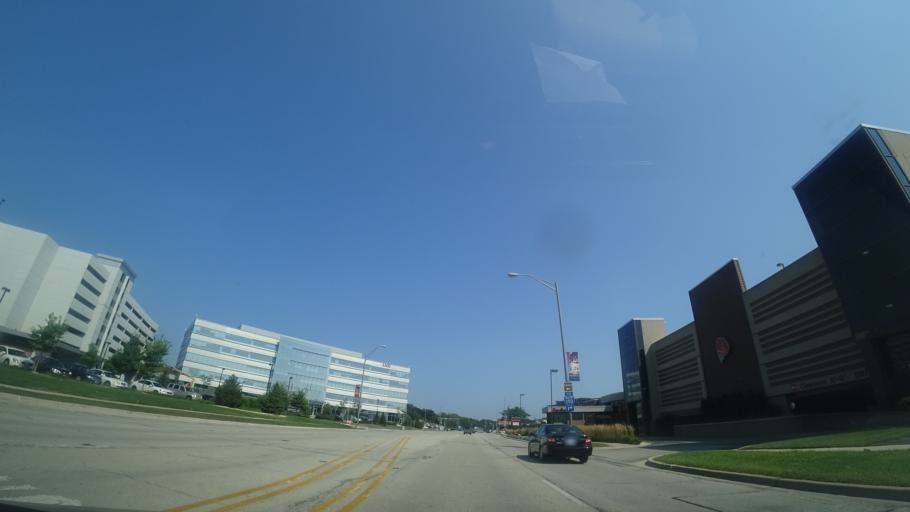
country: US
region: Illinois
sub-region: Cook County
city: Rosemont
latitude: 41.9923
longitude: -87.8628
